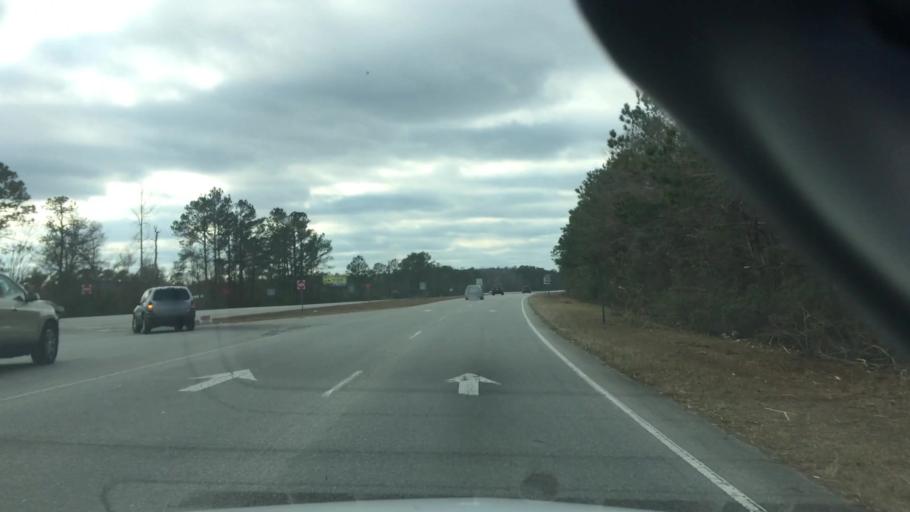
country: US
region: North Carolina
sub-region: Brunswick County
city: Bolivia
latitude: 34.0804
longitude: -78.1395
